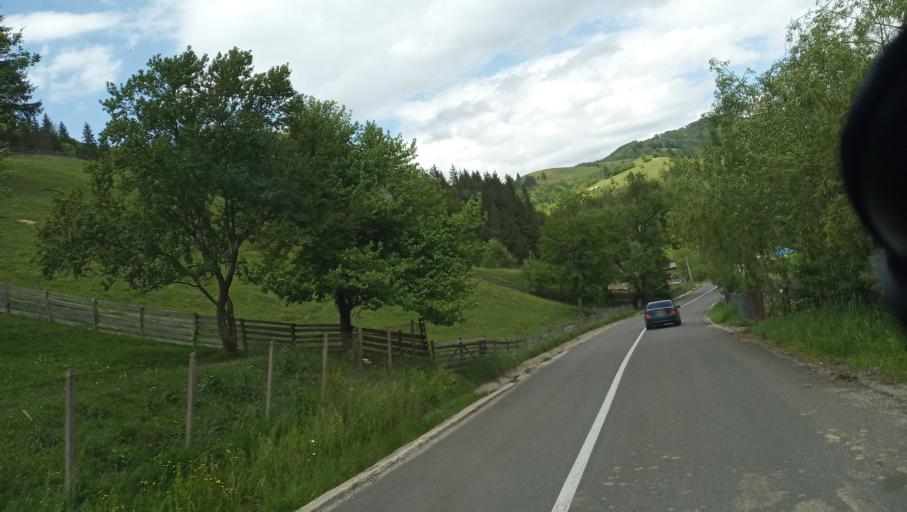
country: RO
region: Alba
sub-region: Comuna Ciuruleasa
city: Ciuruleasa
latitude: 46.2354
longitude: 23.0259
